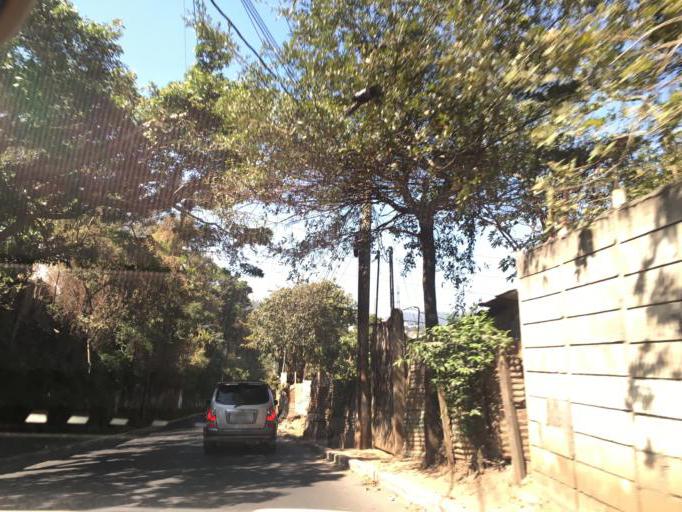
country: GT
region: Guatemala
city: Mixco
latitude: 14.6240
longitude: -90.6033
